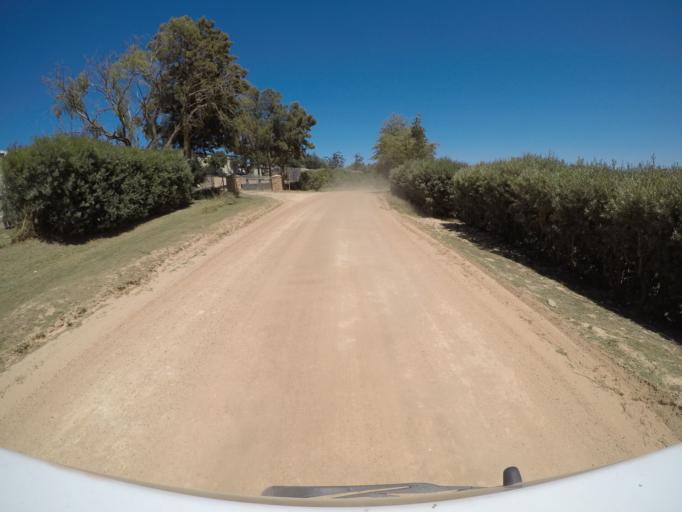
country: ZA
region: Western Cape
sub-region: Overberg District Municipality
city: Grabouw
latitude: -34.2453
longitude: 19.1010
